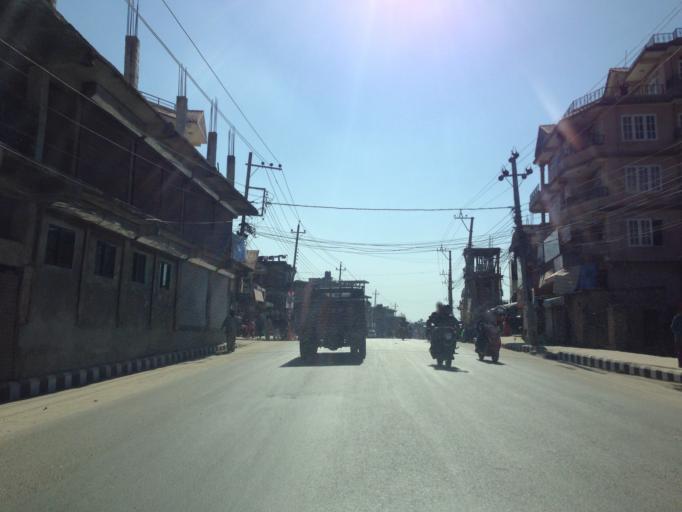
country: NP
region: Central Region
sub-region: Bagmati Zone
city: Kathmandu
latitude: 27.7612
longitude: 85.3521
